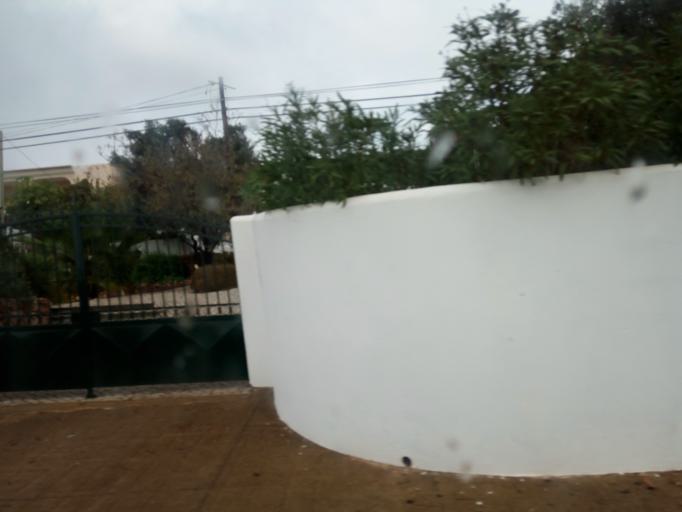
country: PT
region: Faro
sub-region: Faro
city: Santa Barbara de Nexe
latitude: 37.1051
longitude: -7.9840
